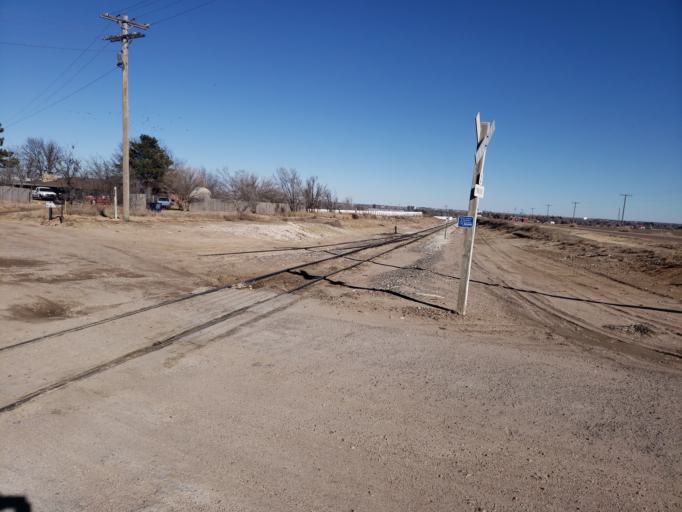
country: US
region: Kansas
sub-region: Ford County
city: Dodge City
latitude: 37.7279
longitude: -100.0517
